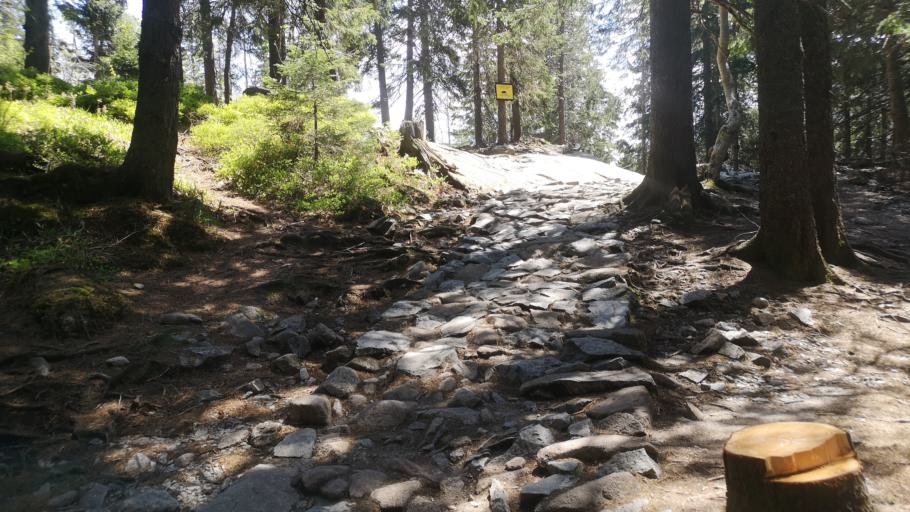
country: SK
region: Presovsky
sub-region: Okres Poprad
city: Vysoke Tatry
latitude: 49.1732
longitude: 20.2195
